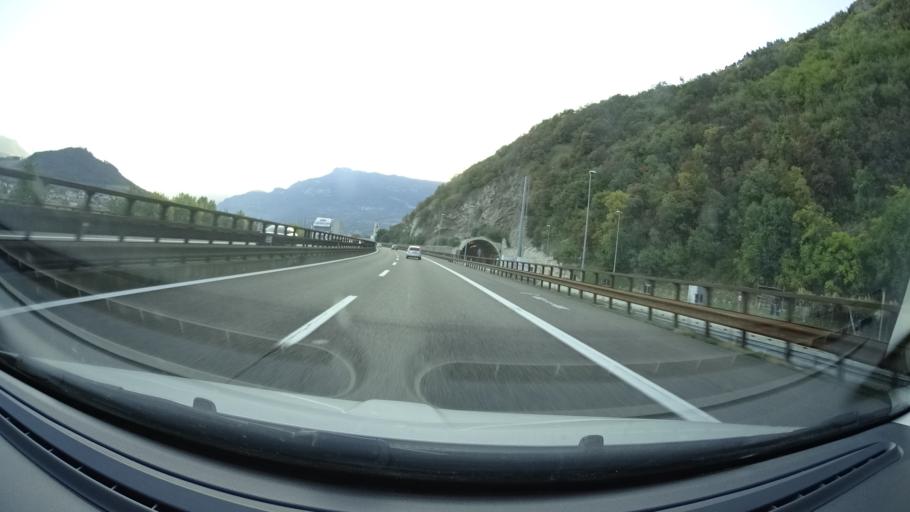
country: IT
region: Trentino-Alto Adige
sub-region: Provincia di Trento
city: Volano
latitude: 45.9275
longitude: 11.0598
